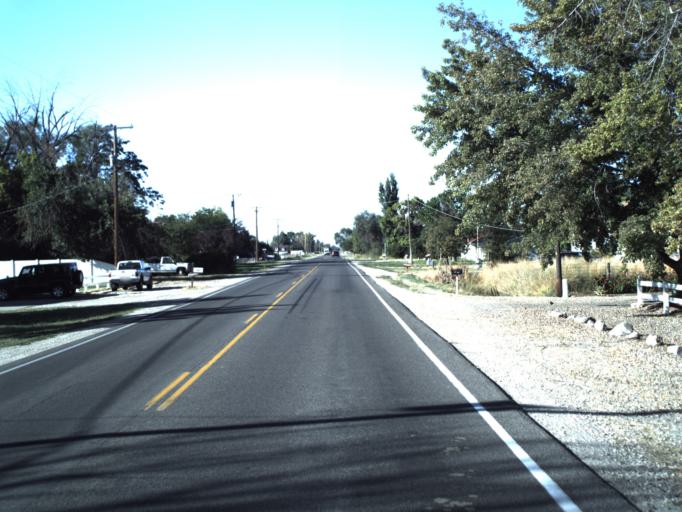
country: US
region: Utah
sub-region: Weber County
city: Hooper
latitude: 41.1775
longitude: -112.1226
